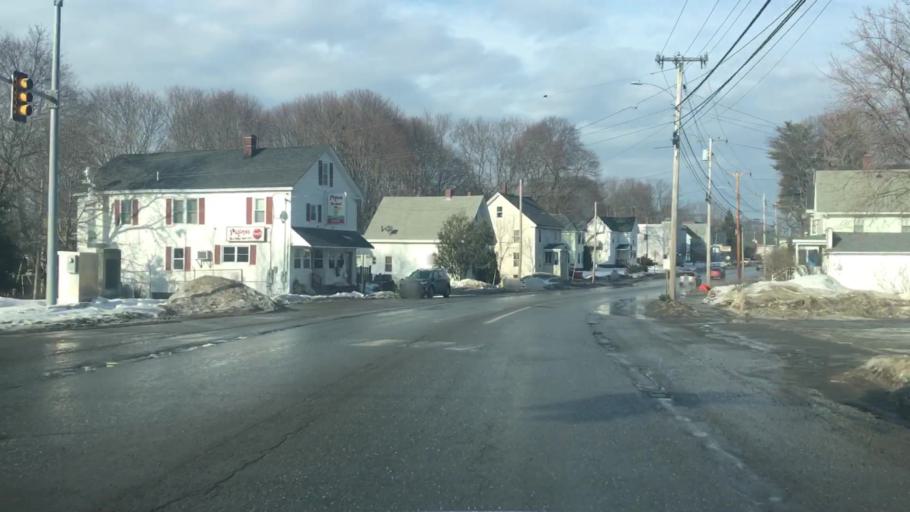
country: US
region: Maine
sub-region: Penobscot County
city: Bangor
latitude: 44.7717
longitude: -68.7803
